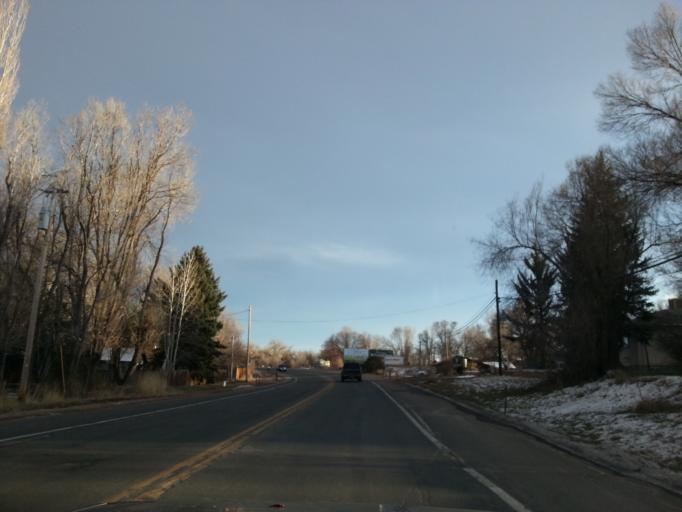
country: US
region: Colorado
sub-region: Larimer County
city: Loveland
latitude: 40.4125
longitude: -105.1685
